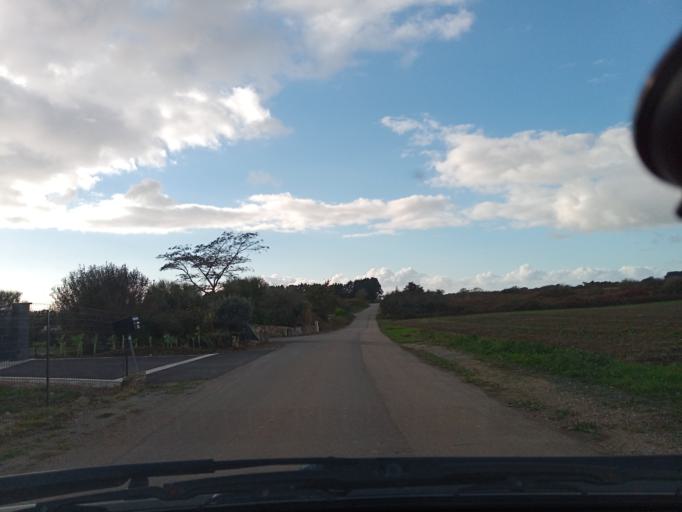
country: FR
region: Brittany
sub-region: Departement du Finistere
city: Plouhinec
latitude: 48.0172
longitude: -4.4944
